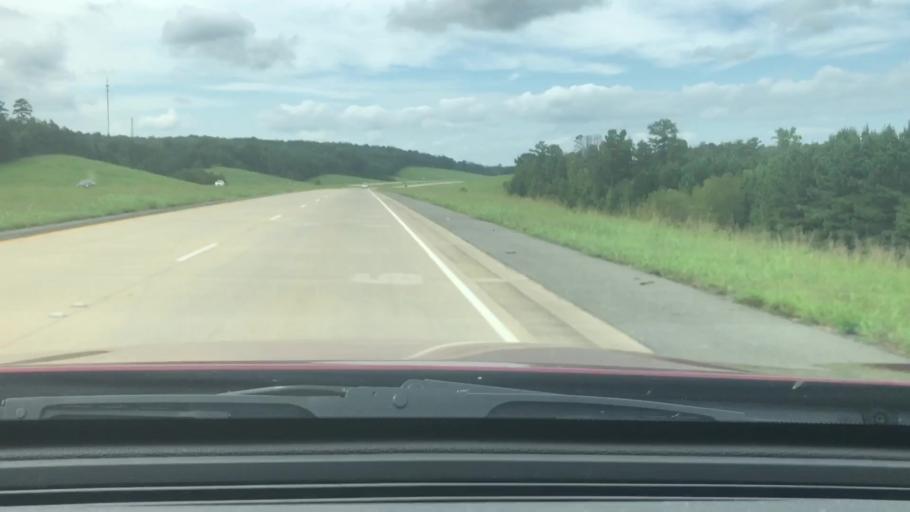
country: US
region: Louisiana
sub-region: Caddo Parish
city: Vivian
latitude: 32.9238
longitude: -93.8884
